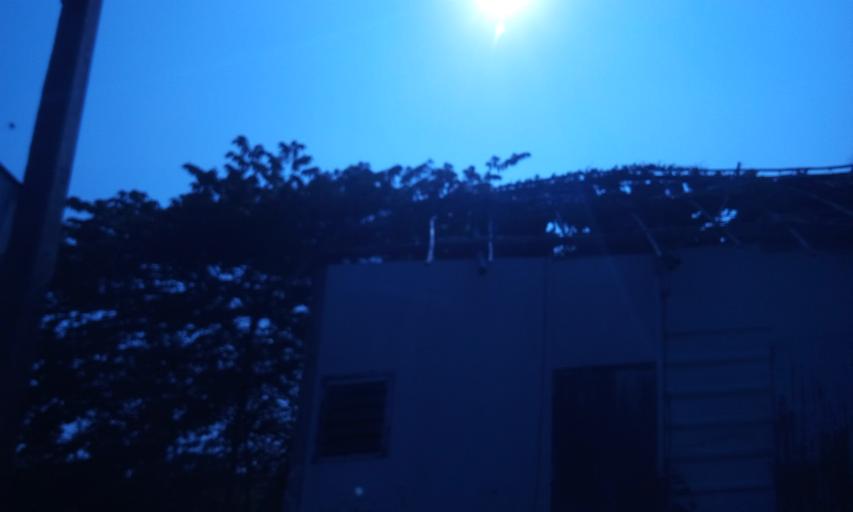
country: TH
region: Pathum Thani
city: Lam Luk Ka
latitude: 13.9626
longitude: 100.7059
